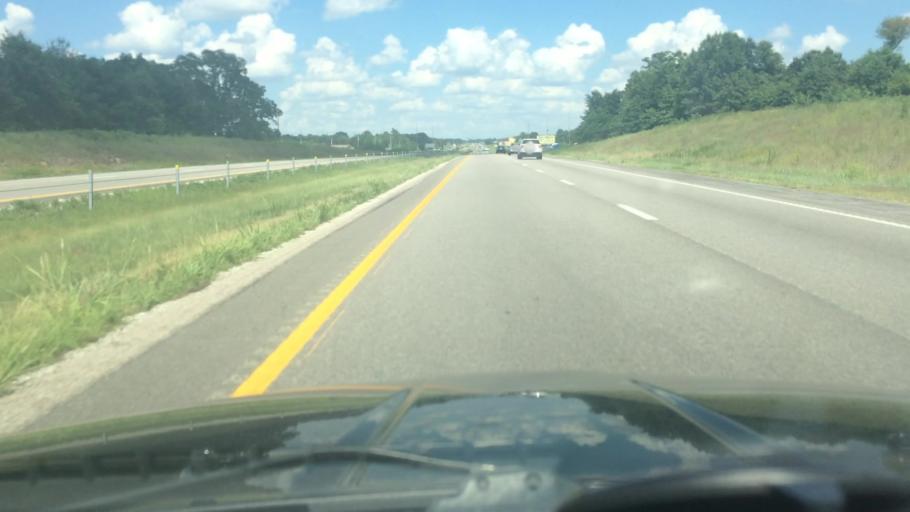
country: US
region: Missouri
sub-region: Greene County
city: Strafford
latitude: 37.2527
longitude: -93.1755
